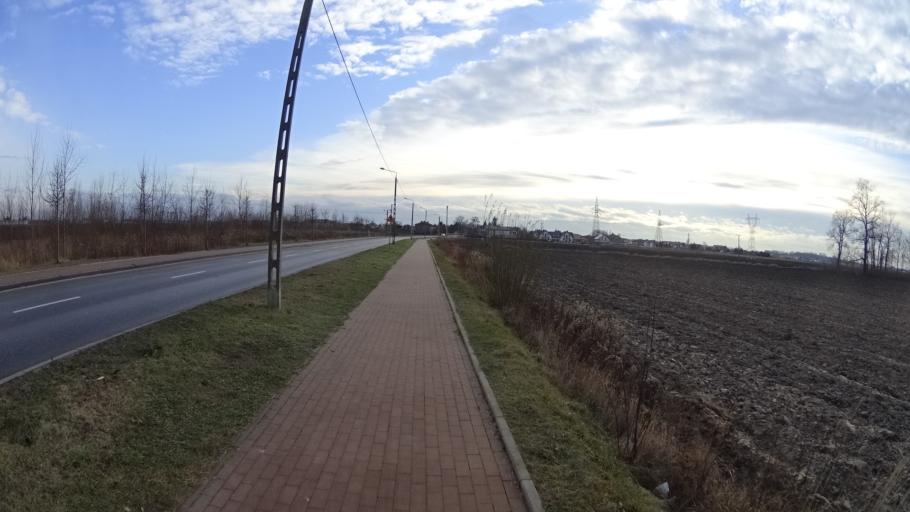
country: PL
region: Masovian Voivodeship
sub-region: Powiat warszawski zachodni
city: Ozarow Mazowiecki
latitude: 52.2293
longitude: 20.8023
